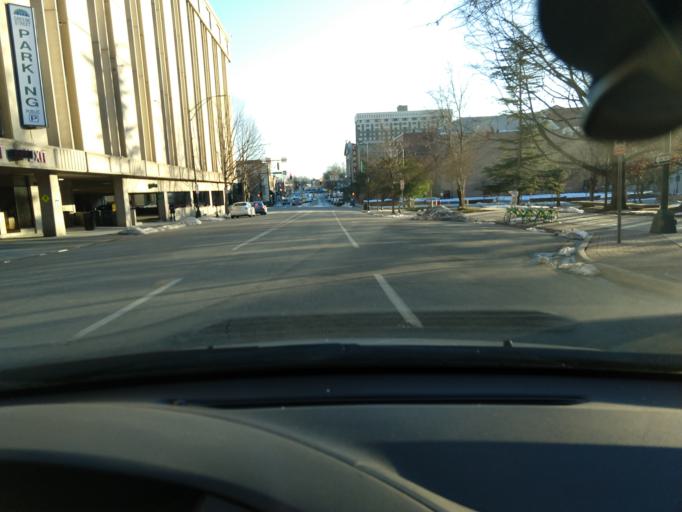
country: US
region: North Carolina
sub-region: Guilford County
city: Greensboro
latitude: 36.0711
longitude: -79.7917
